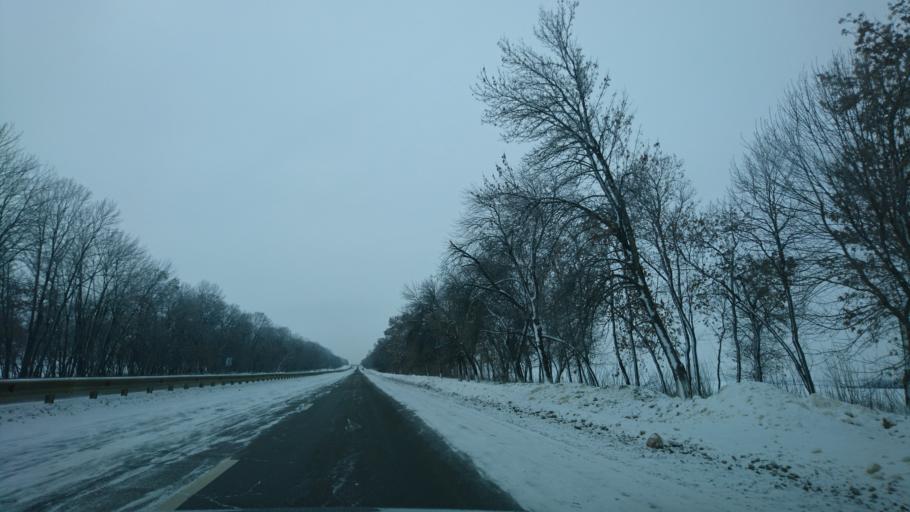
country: RU
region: Belgorod
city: Mayskiy
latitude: 50.4310
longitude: 36.3859
